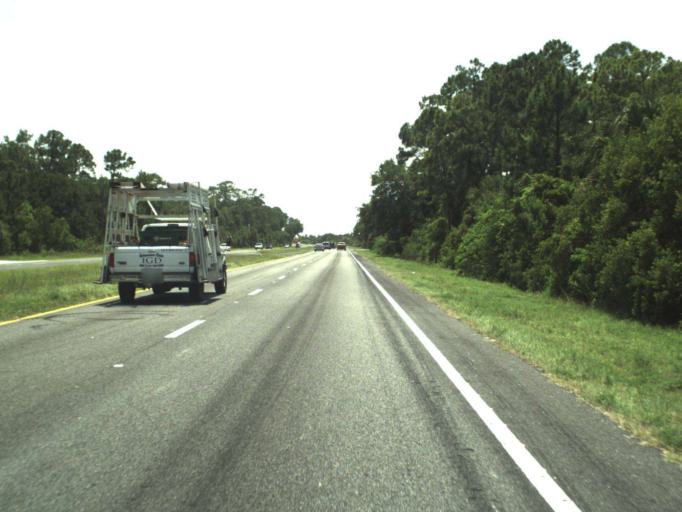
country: US
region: Florida
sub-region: Volusia County
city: Ponce Inlet
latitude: 29.0974
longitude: -80.9707
